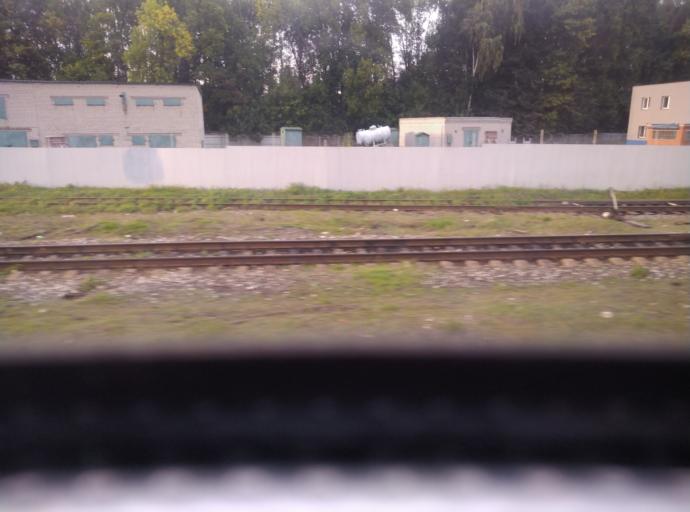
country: RU
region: Jaroslavl
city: Yaroslavl
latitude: 57.5981
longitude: 39.8540
